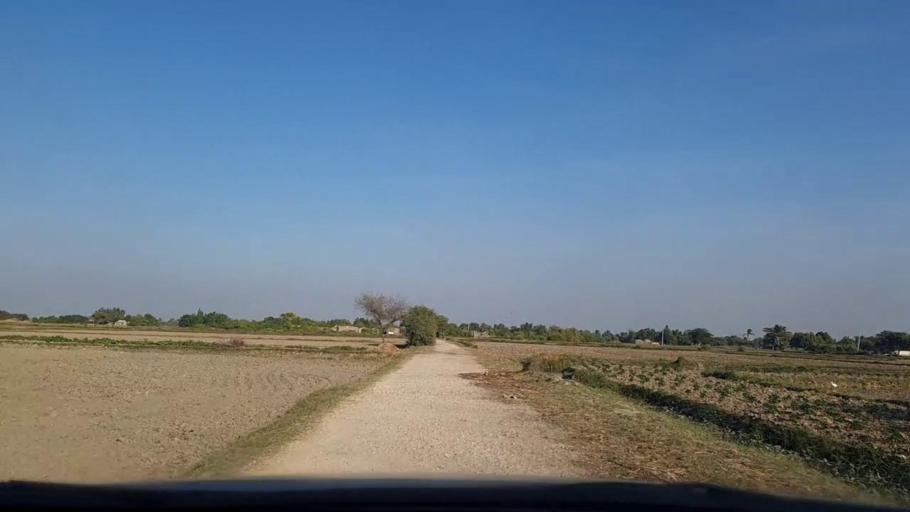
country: PK
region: Sindh
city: Mirpur Sakro
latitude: 24.5163
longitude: 67.6438
